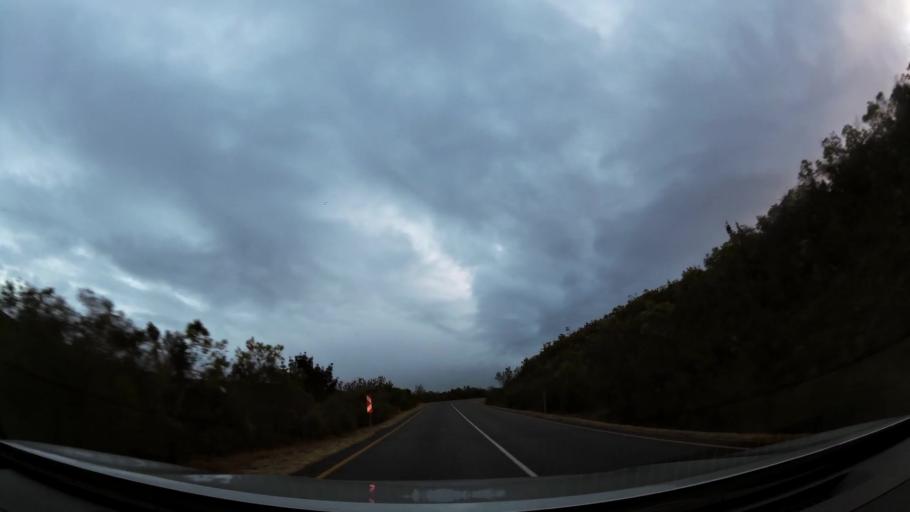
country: ZA
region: Western Cape
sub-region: Overberg District Municipality
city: Swellendam
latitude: -33.9868
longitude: 20.7169
